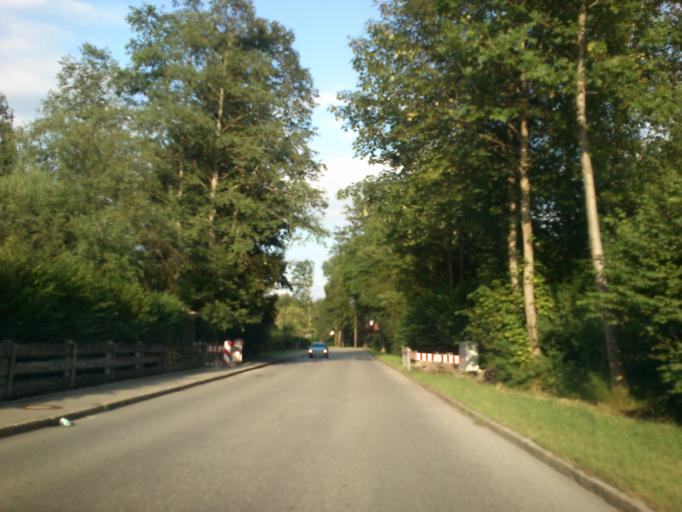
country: DE
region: Bavaria
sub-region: Upper Bavaria
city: Grainau
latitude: 47.4802
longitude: 11.0393
